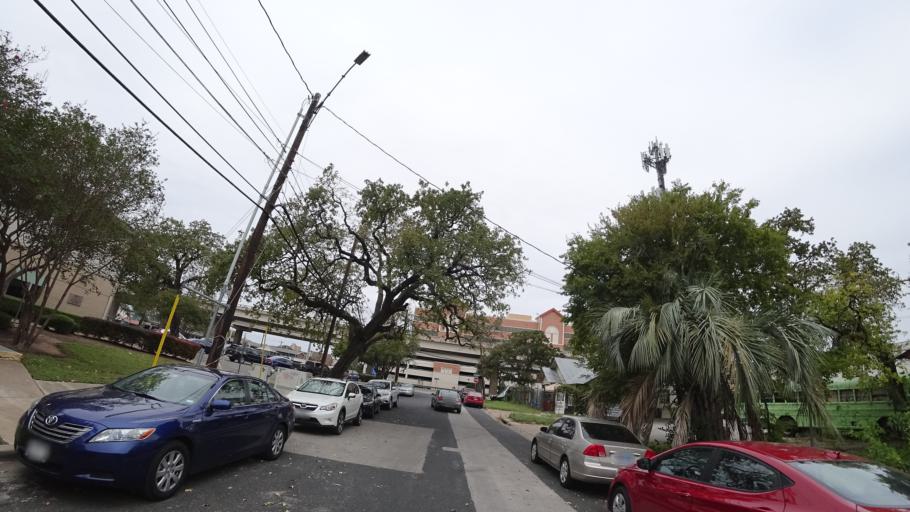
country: US
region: Texas
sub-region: Travis County
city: Austin
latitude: 30.2877
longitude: -97.7231
